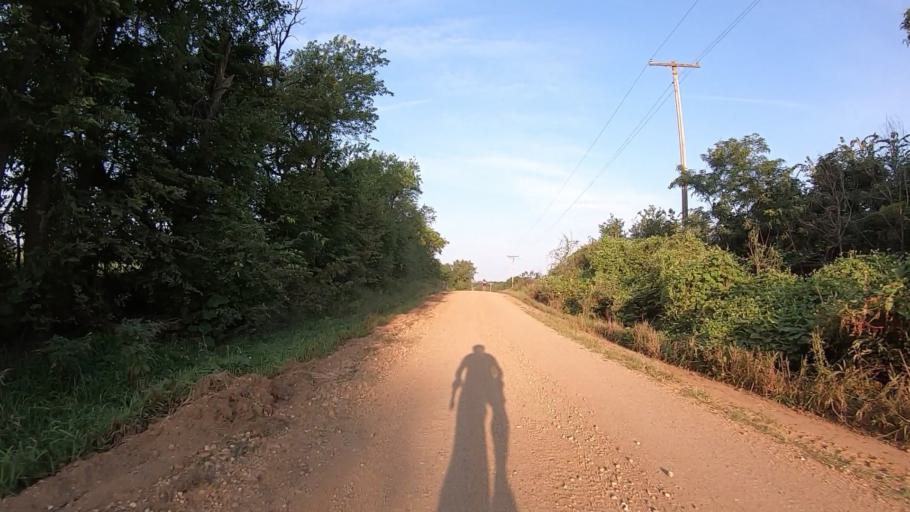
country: US
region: Kansas
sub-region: Marshall County
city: Marysville
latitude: 39.7694
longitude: -96.7497
